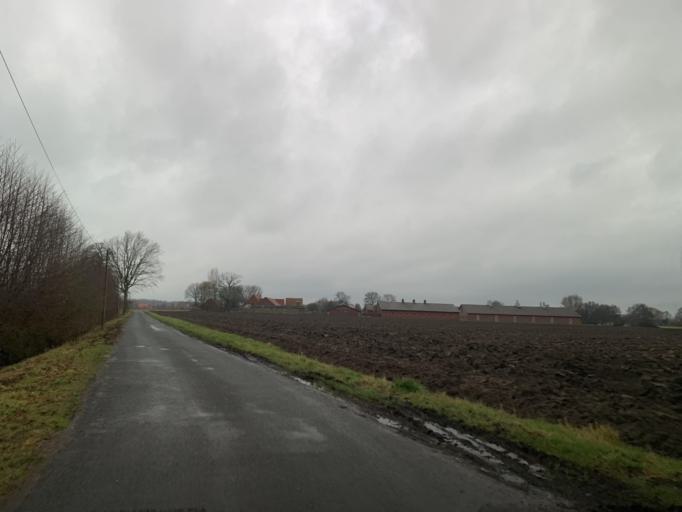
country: DE
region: North Rhine-Westphalia
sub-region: Regierungsbezirk Munster
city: Nordwalde
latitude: 52.0858
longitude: 7.5150
